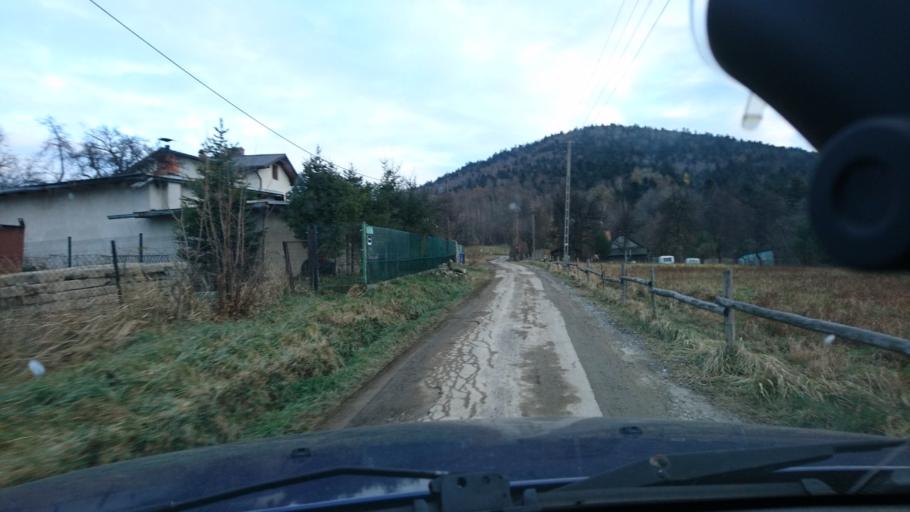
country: PL
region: Silesian Voivodeship
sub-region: Powiat bielski
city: Wilkowice
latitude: 49.7936
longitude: 19.0833
